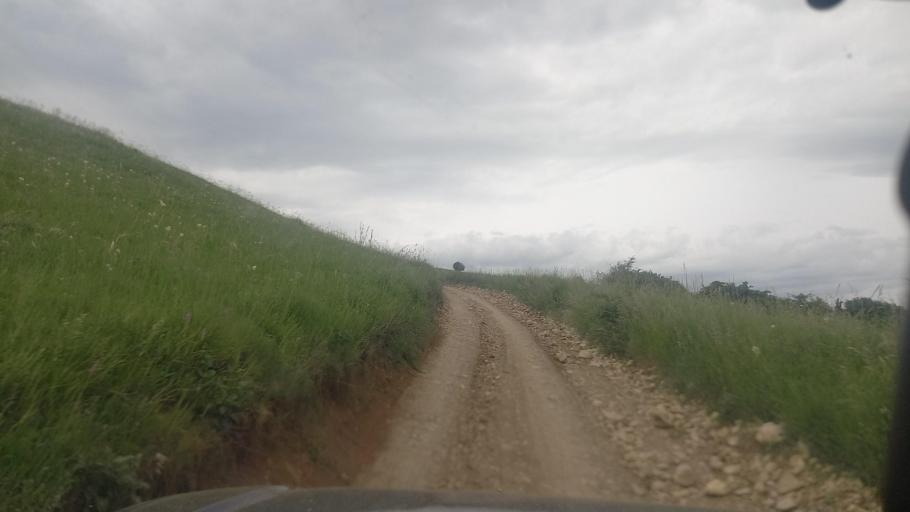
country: RU
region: Krasnodarskiy
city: Peredovaya
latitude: 44.0764
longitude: 41.3636
